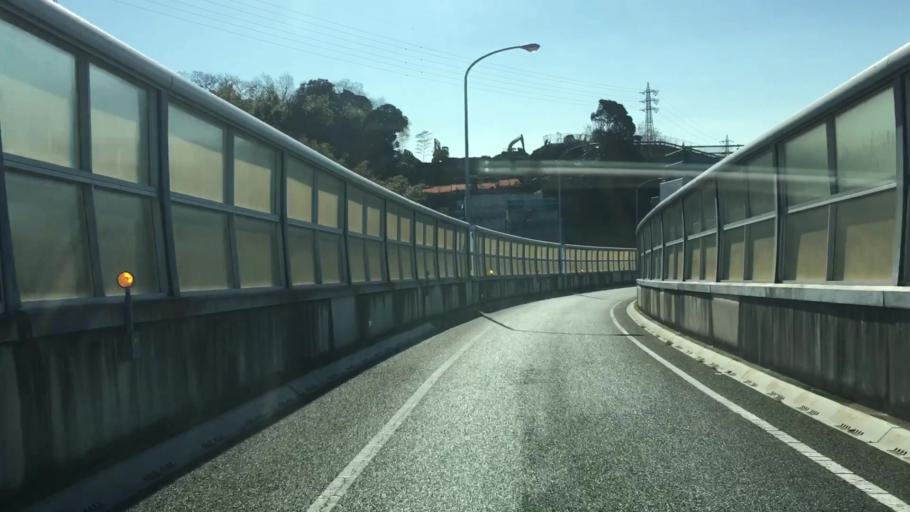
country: JP
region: Kanagawa
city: Miura
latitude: 35.2134
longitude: 139.6373
